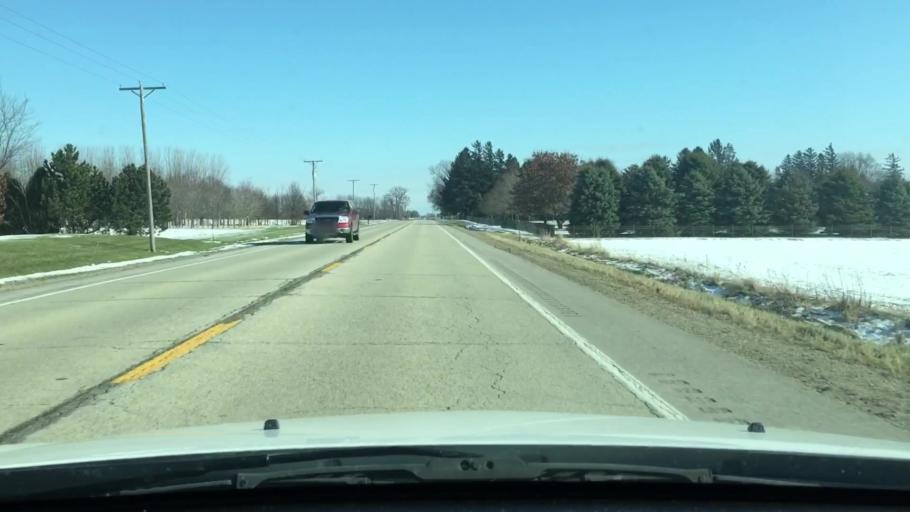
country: US
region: Illinois
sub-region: DeKalb County
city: Malta
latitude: 42.0015
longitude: -88.8105
